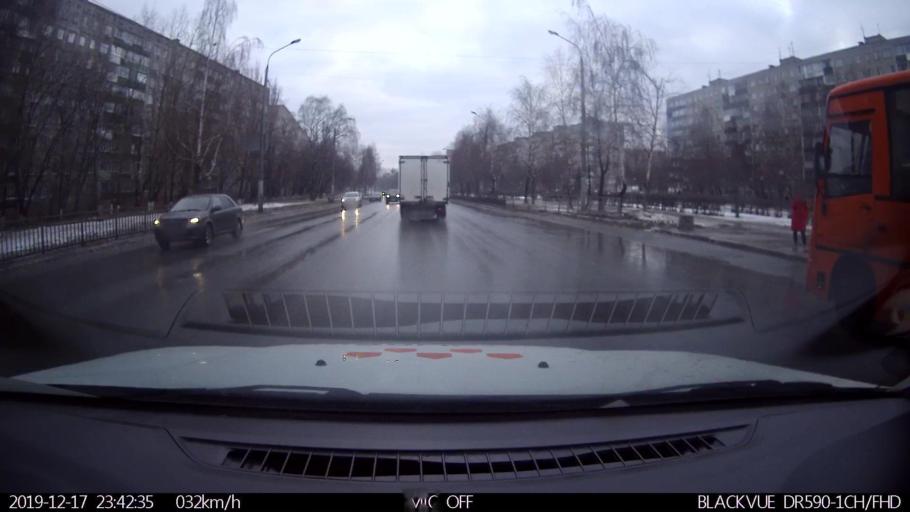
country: RU
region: Nizjnij Novgorod
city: Gorbatovka
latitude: 56.3635
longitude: 43.8173
